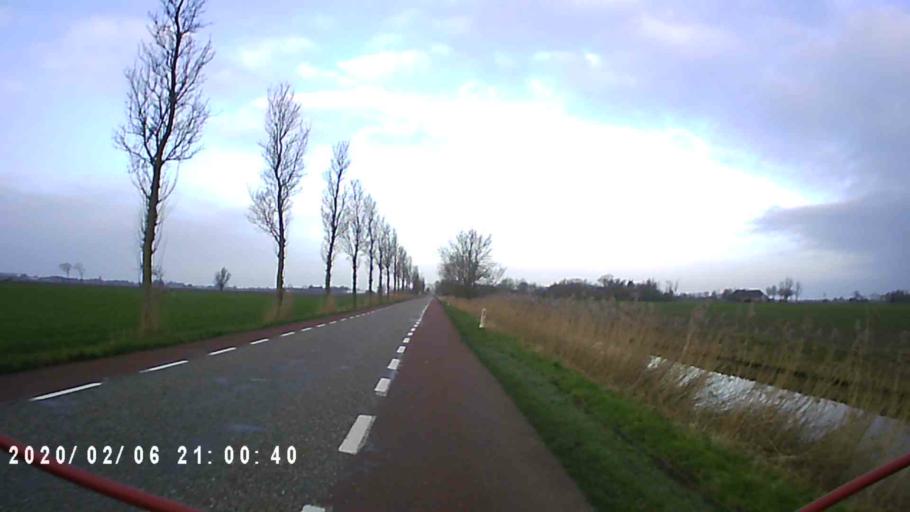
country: NL
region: Groningen
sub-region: Gemeente Zuidhorn
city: Oldehove
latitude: 53.3108
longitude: 6.4272
